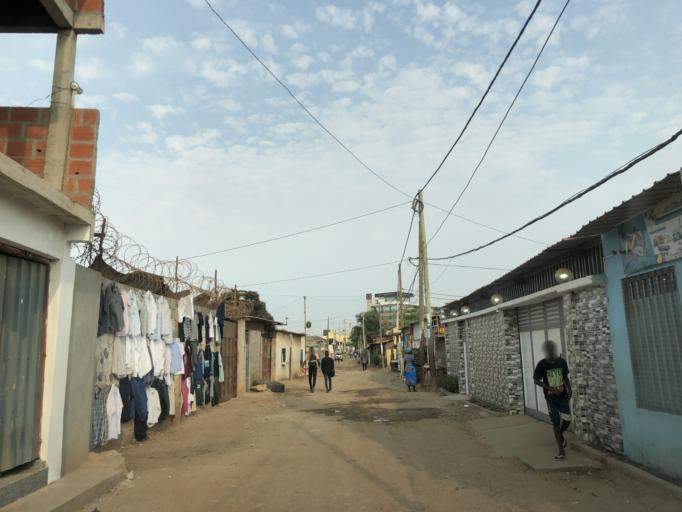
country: AO
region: Luanda
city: Luanda
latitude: -8.9120
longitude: 13.1731
